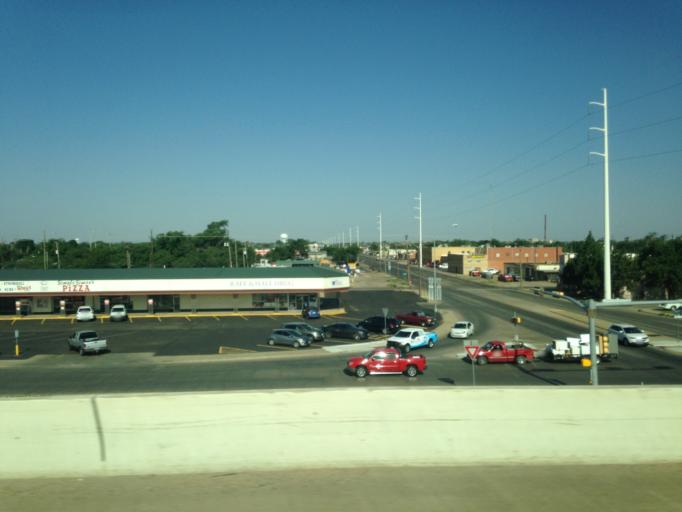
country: US
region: Texas
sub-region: Lubbock County
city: Lubbock
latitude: 33.5633
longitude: -101.8451
